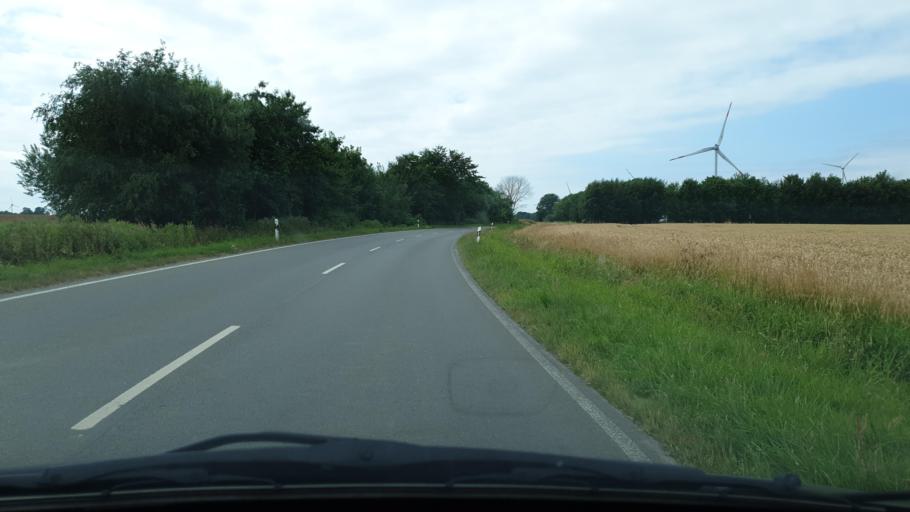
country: DE
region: Schleswig-Holstein
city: Marnerdeich
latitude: 53.9482
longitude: 8.9782
